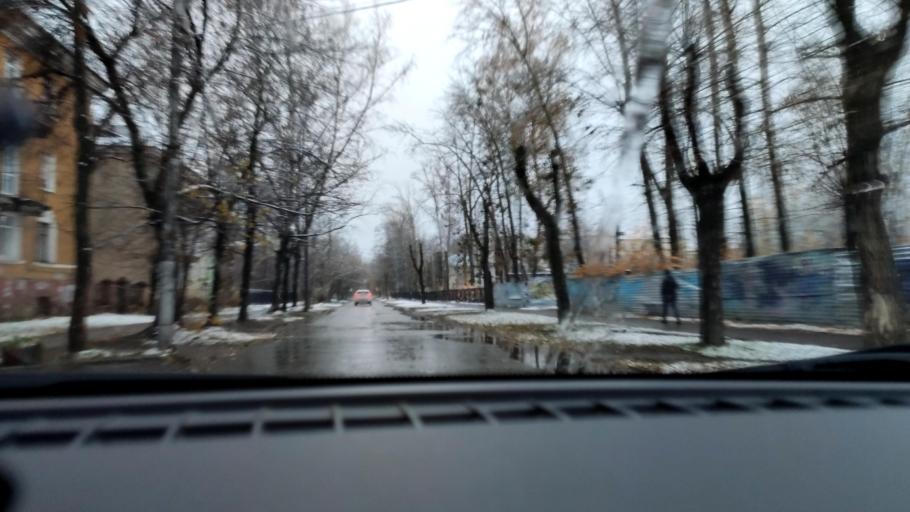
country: RU
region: Perm
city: Kultayevo
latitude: 58.0006
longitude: 55.9468
